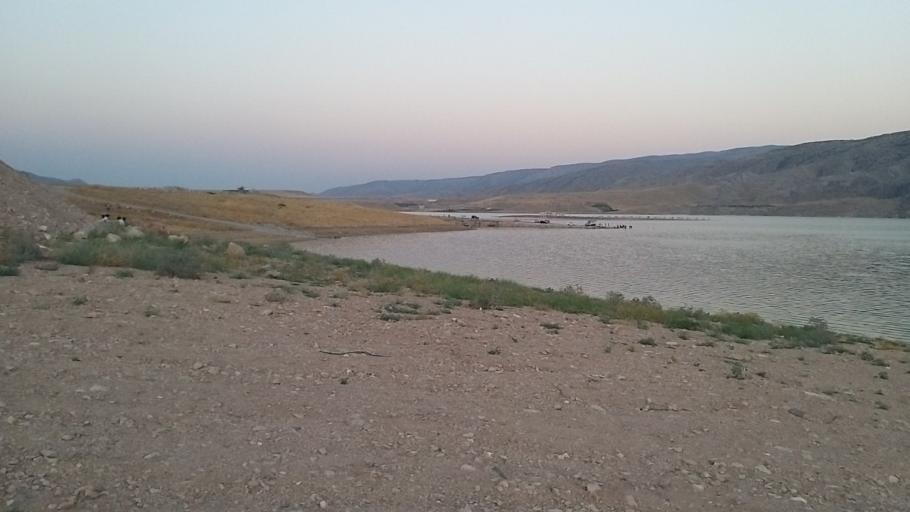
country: TR
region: Batman
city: Hasankeyf
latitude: 37.7237
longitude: 41.4147
